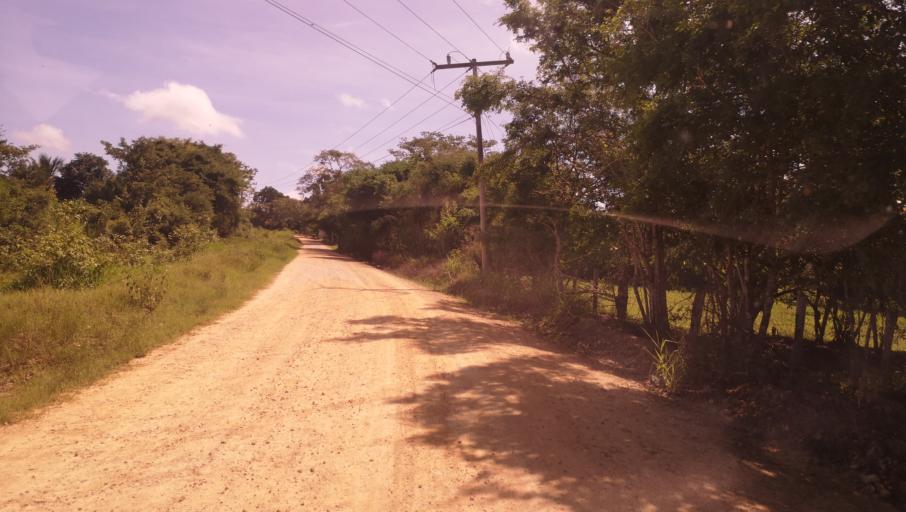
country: GT
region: Peten
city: Melchor de Mencos
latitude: 16.9279
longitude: -89.2791
